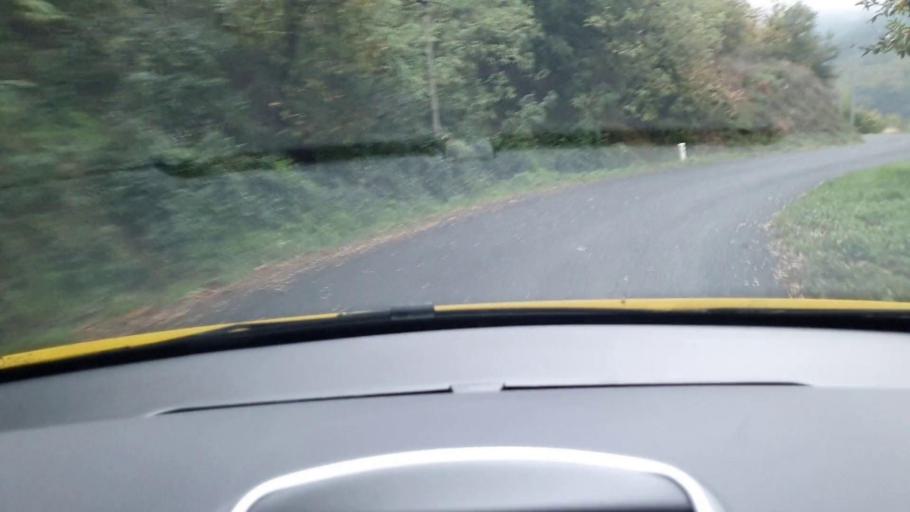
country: FR
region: Languedoc-Roussillon
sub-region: Departement du Gard
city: Sumene
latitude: 44.0320
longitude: 3.7333
